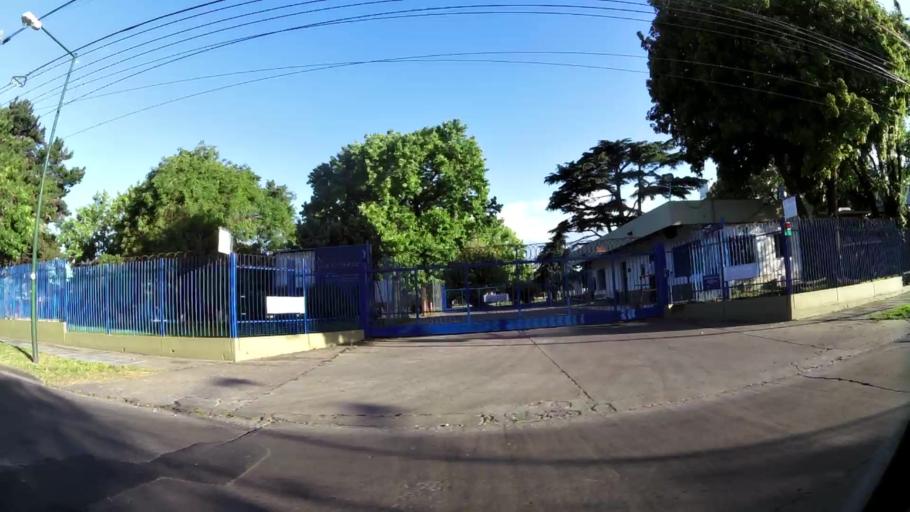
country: AR
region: Buenos Aires
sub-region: Partido de San Isidro
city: San Isidro
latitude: -34.4714
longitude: -58.5487
